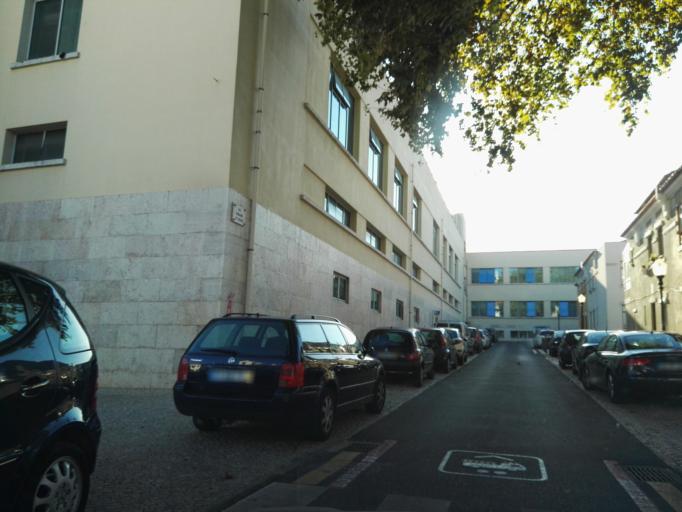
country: PT
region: Lisbon
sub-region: Lisbon
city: Lisbon
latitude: 38.7404
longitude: -9.1385
